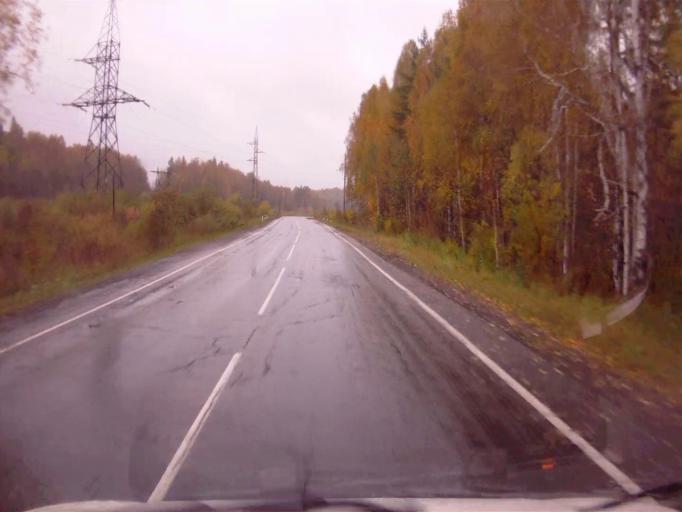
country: RU
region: Chelyabinsk
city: Verkhniy Ufaley
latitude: 55.9439
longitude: 60.4074
